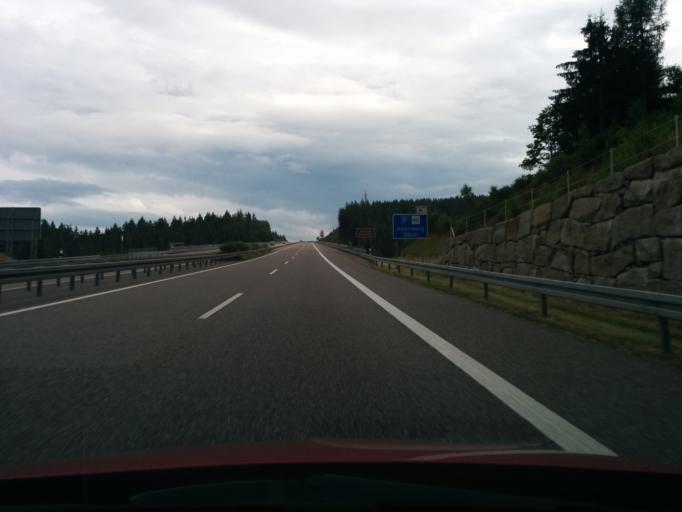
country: DE
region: Thuringia
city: Sankt Kilian
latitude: 50.5678
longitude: 10.7298
